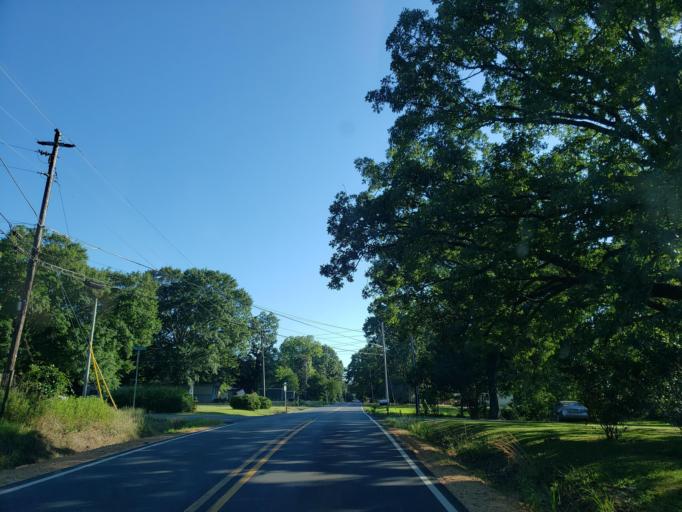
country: US
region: Georgia
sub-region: Floyd County
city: Shannon
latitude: 34.3414
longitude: -85.1509
